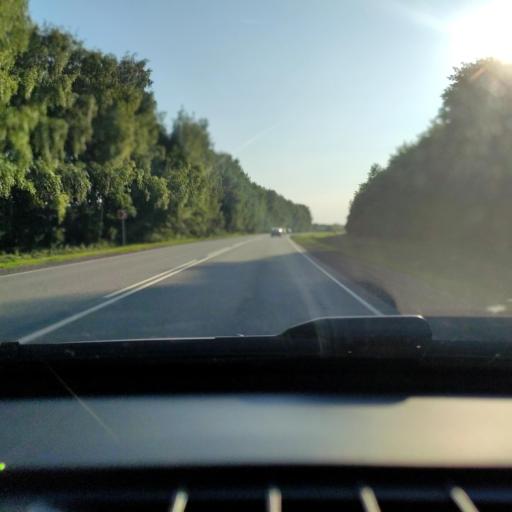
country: RU
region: Voronezj
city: Kashirskoye
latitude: 51.4581
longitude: 39.8202
